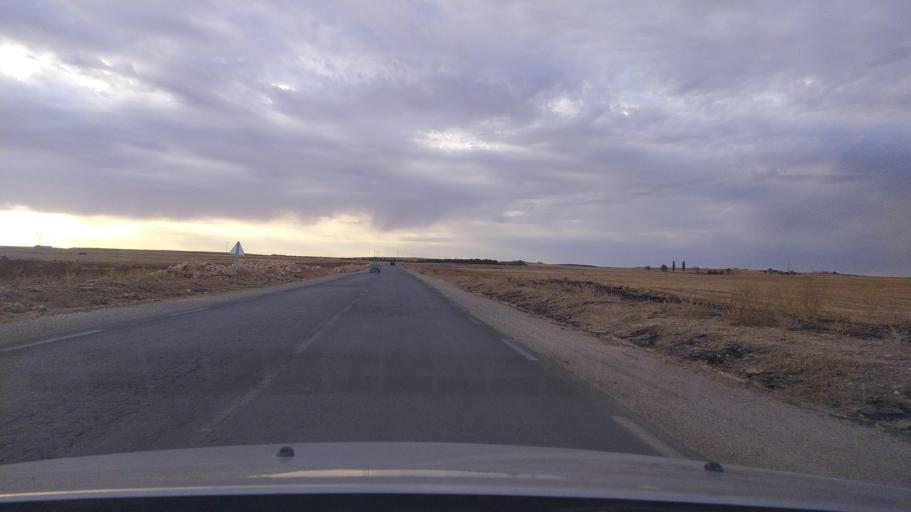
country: DZ
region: Tiaret
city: Frenda
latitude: 34.9805
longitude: 1.1495
